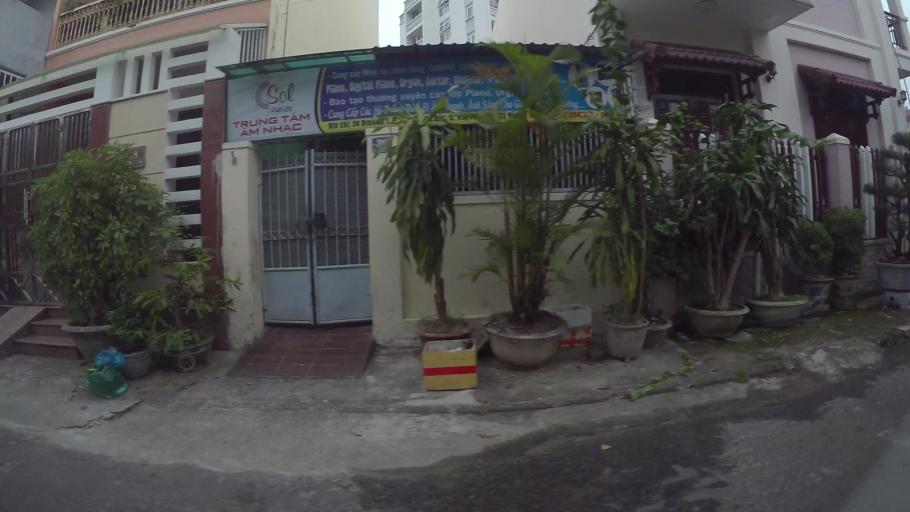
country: VN
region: Da Nang
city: Cam Le
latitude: 16.0418
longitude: 108.2079
